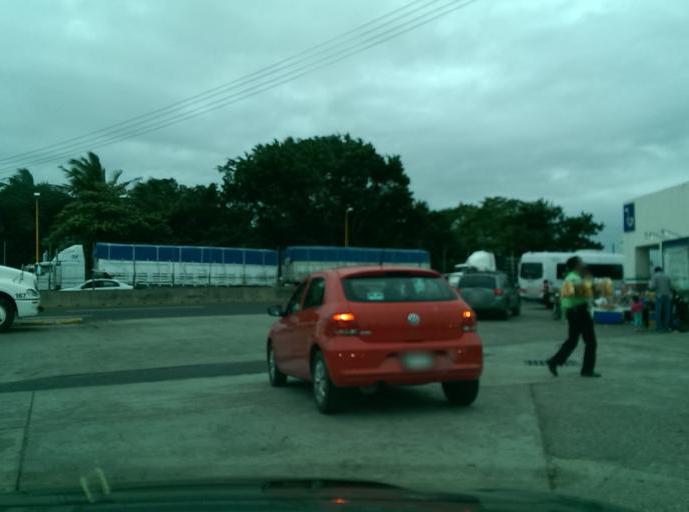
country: MX
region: Veracruz
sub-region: Chacaltianguis
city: Chacaltianguis
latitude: 18.3340
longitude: -95.8195
